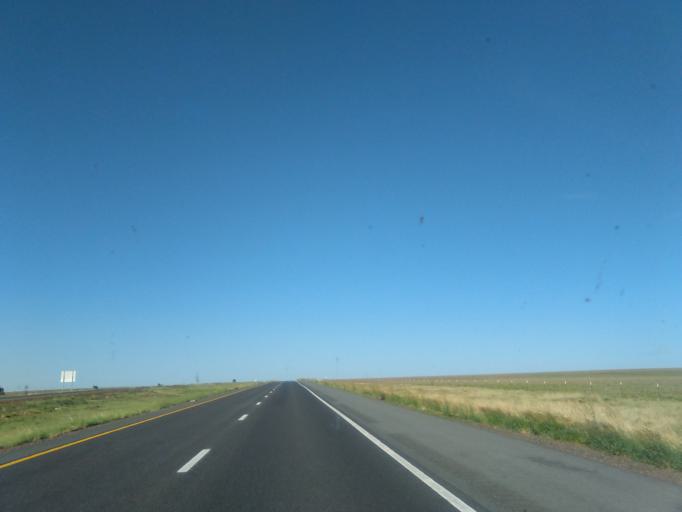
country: US
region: New Mexico
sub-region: San Miguel County
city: Las Vegas
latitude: 35.6846
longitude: -105.1498
